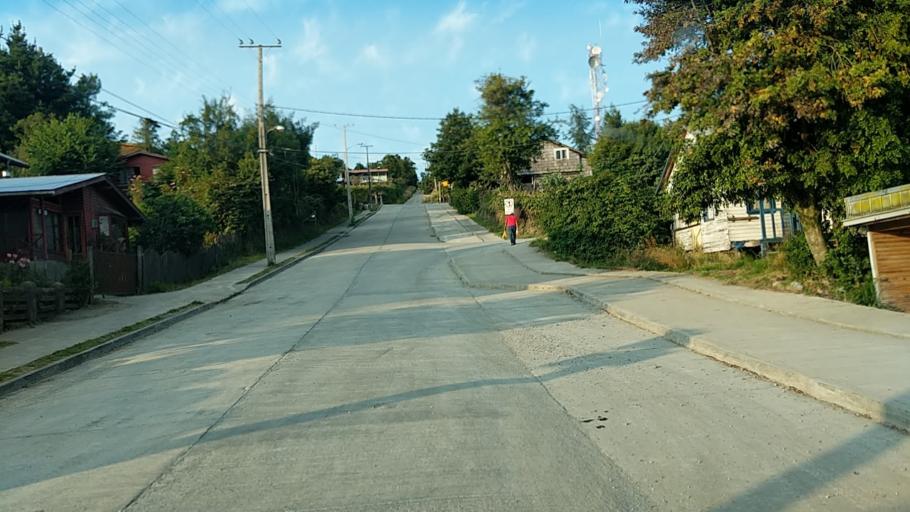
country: CL
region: Los Lagos
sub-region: Provincia de Llanquihue
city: La Ensenada
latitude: -41.4936
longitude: -72.3084
